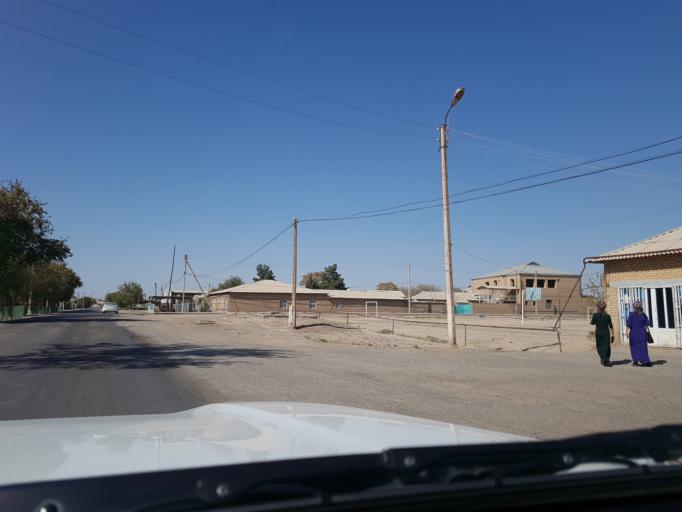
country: IR
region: Razavi Khorasan
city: Sarakhs
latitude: 36.5196
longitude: 61.2191
